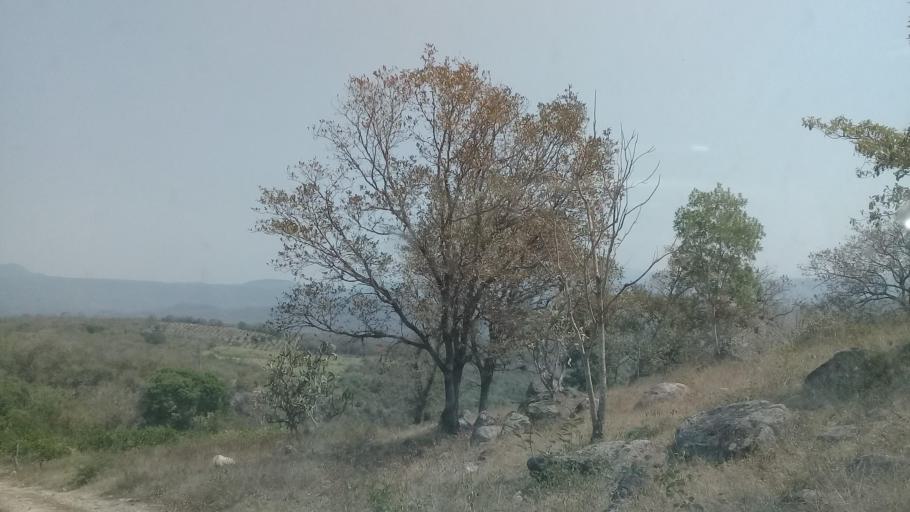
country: MX
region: Veracruz
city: El Castillo
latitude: 19.5699
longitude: -96.8059
